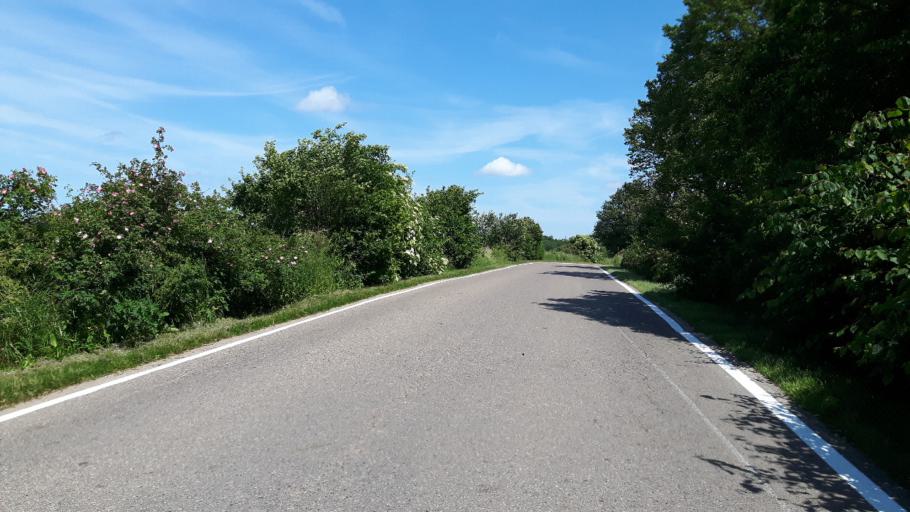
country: PL
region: Pomeranian Voivodeship
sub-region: Powiat wejherowski
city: Gniewino
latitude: 54.7249
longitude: 17.9712
